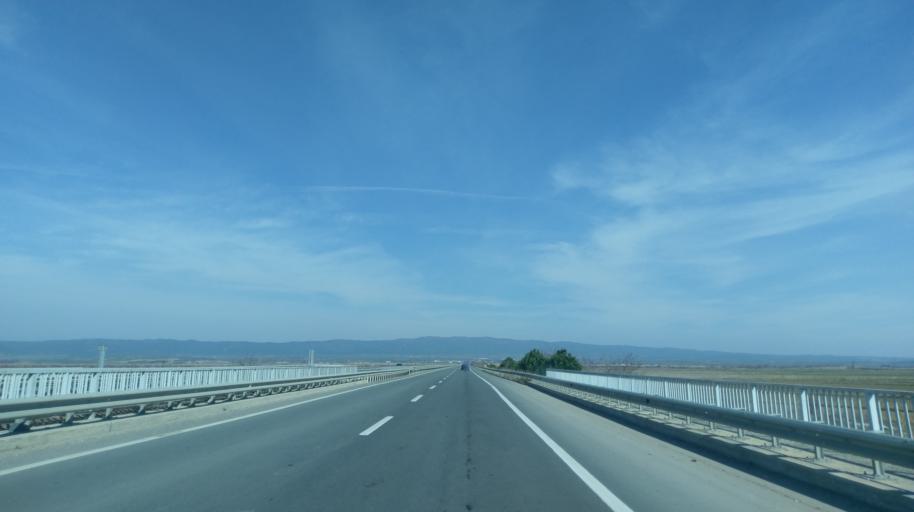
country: TR
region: Canakkale
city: Evrese
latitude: 40.6073
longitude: 26.8644
